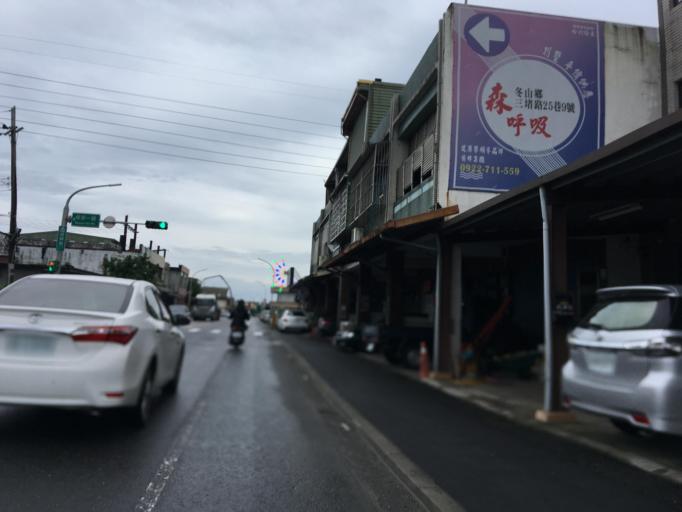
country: TW
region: Taiwan
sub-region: Yilan
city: Yilan
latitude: 24.6385
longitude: 121.7989
